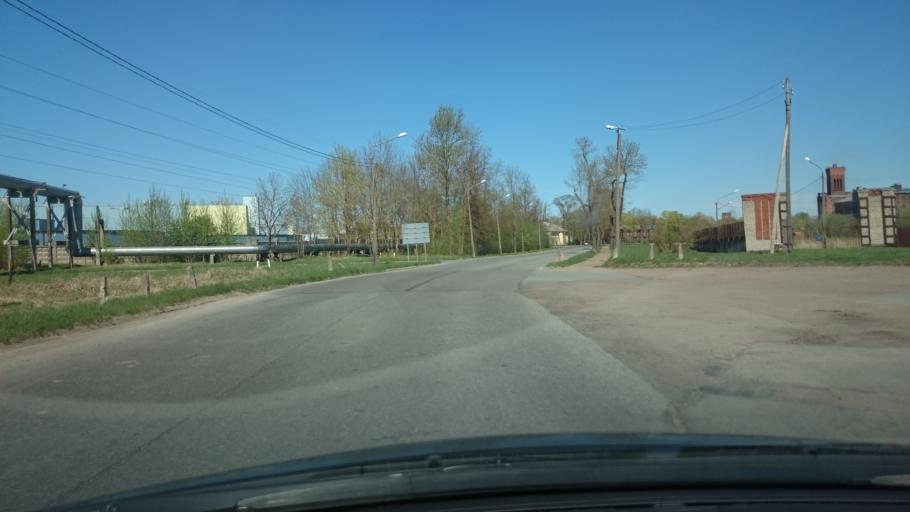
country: EE
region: Ida-Virumaa
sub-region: Narva linn
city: Narva
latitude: 59.3567
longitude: 28.1840
